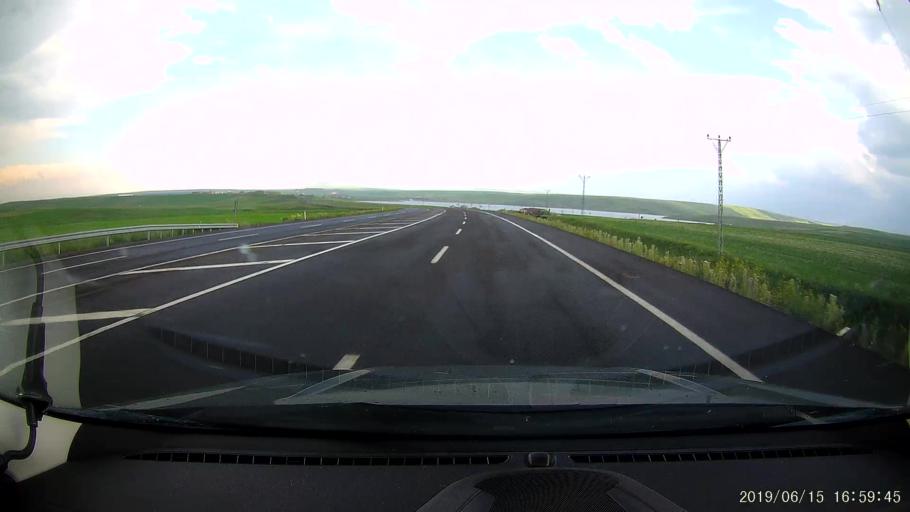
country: TR
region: Kars
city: Susuz
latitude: 40.7476
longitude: 43.1528
